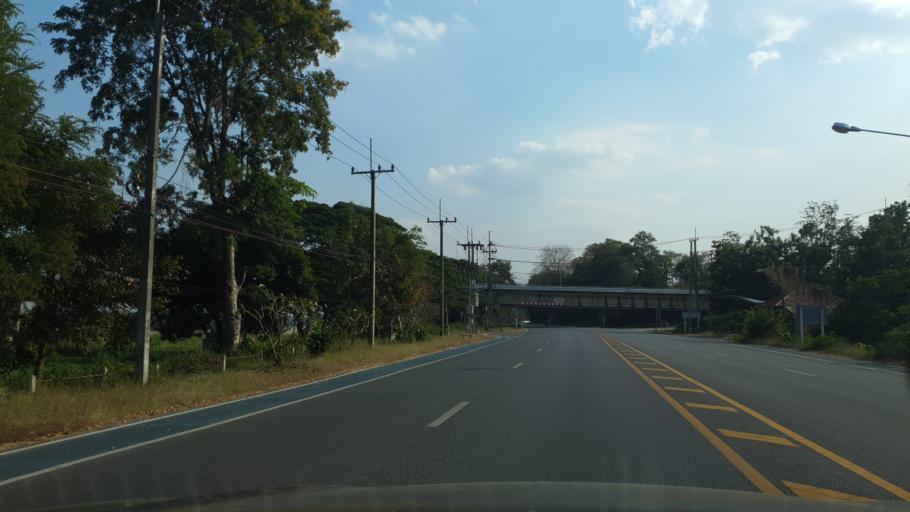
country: TH
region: Tak
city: Tak
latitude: 16.8568
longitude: 99.1221
